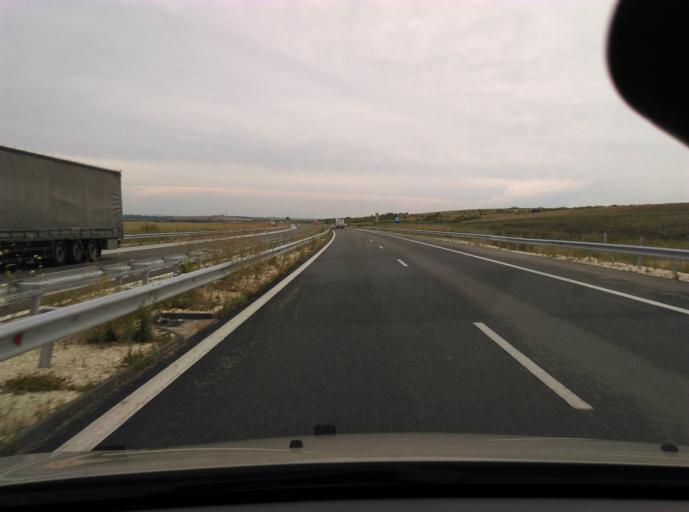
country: BG
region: Stara Zagora
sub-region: Obshtina Chirpan
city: Chirpan
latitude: 42.1179
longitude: 25.3976
